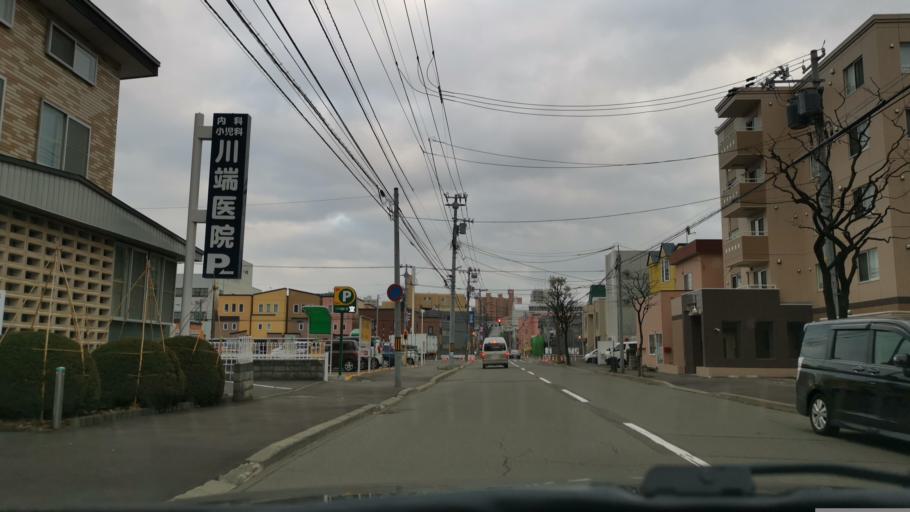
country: JP
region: Hokkaido
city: Sapporo
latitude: 43.0507
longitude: 141.3925
